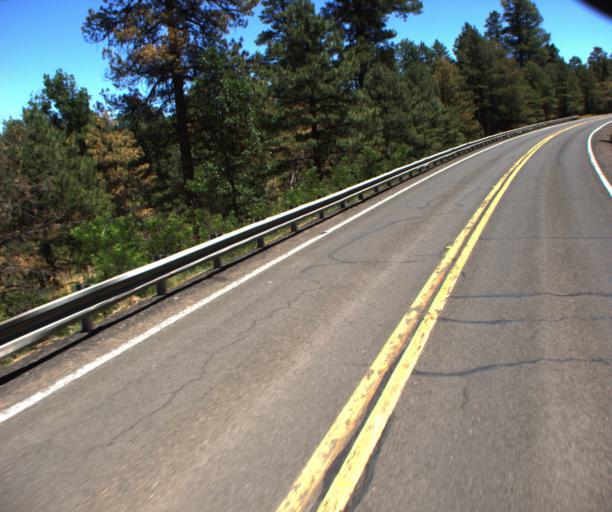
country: US
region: Arizona
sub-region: Gila County
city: Pine
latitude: 34.6066
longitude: -111.2288
